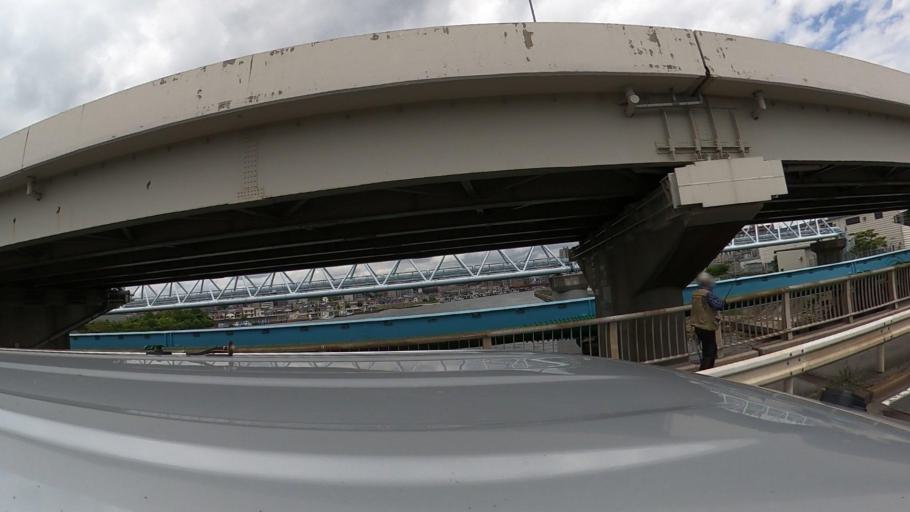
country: JP
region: Kanagawa
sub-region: Kawasaki-shi
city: Kawasaki
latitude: 35.4943
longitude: 139.6784
